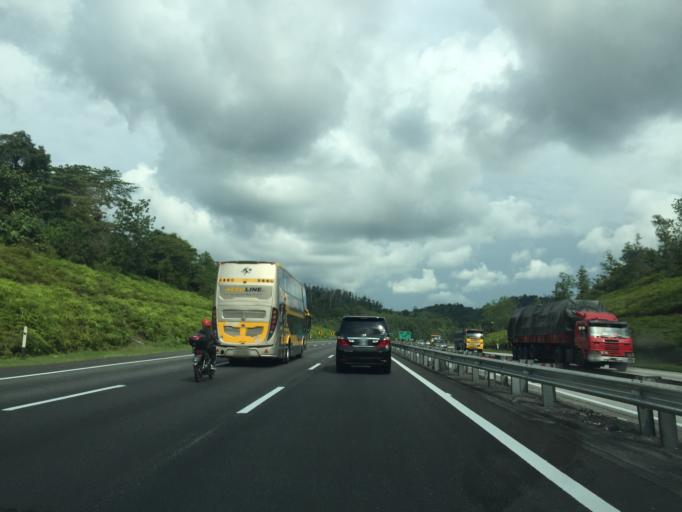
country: MY
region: Selangor
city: Batang Berjuntai
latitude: 3.5901
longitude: 101.5189
